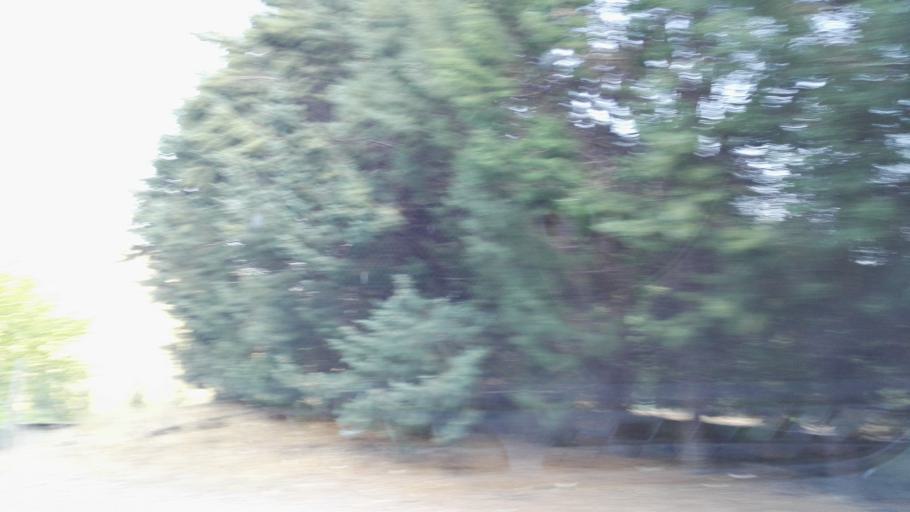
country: IT
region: Calabria
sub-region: Provincia di Reggio Calabria
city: Caulonia
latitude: 38.4147
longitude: 16.3733
